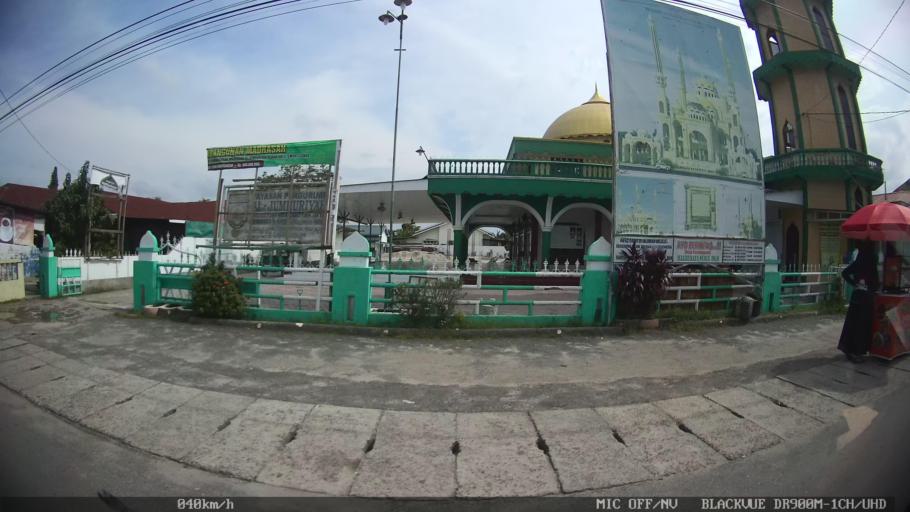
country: ID
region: North Sumatra
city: Percut
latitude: 3.6071
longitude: 98.7800
